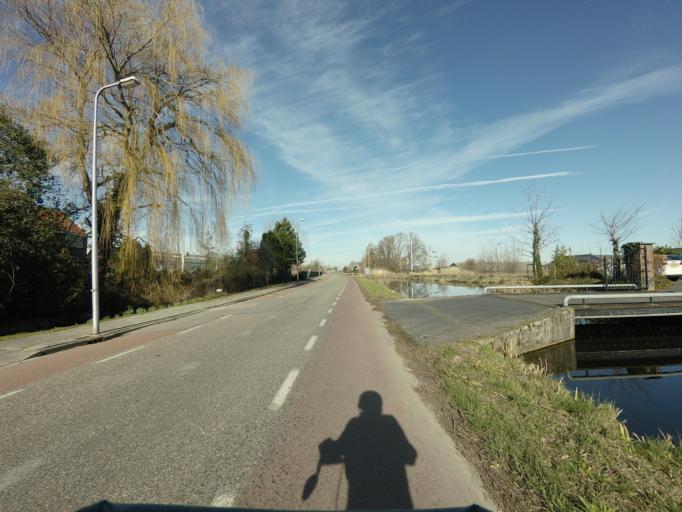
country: NL
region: South Holland
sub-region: Gemeente Kaag en Braassem
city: Leimuiden
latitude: 52.2028
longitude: 4.6696
